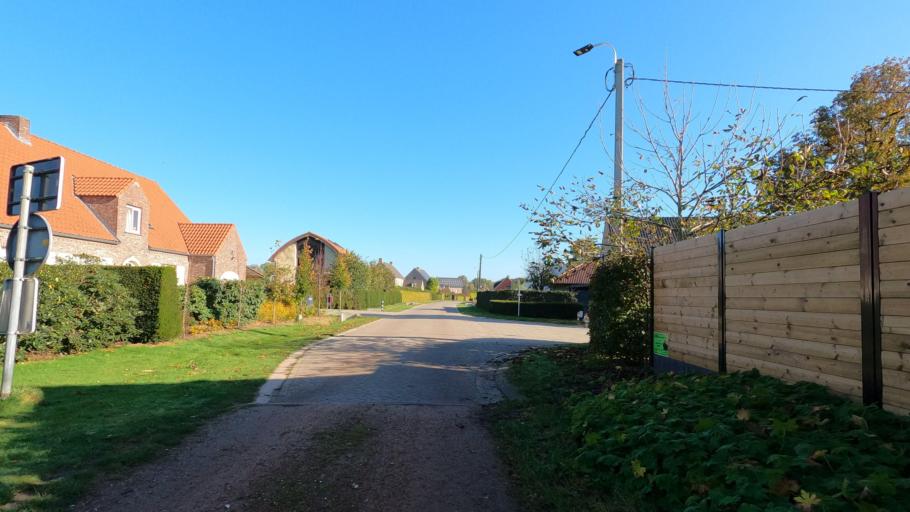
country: BE
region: Flanders
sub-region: Provincie Antwerpen
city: Oostmalle
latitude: 51.3050
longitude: 4.7246
